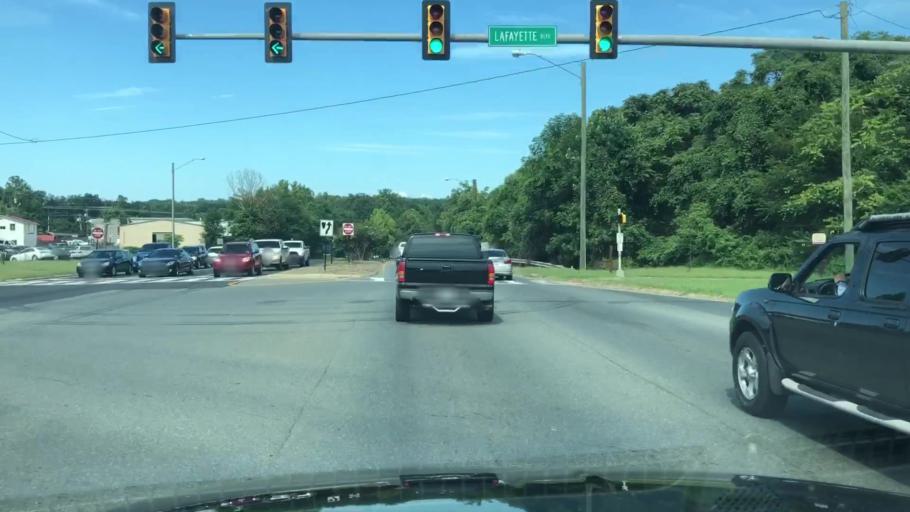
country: US
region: Virginia
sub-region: City of Fredericksburg
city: Fredericksburg
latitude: 38.2905
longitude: -77.4727
